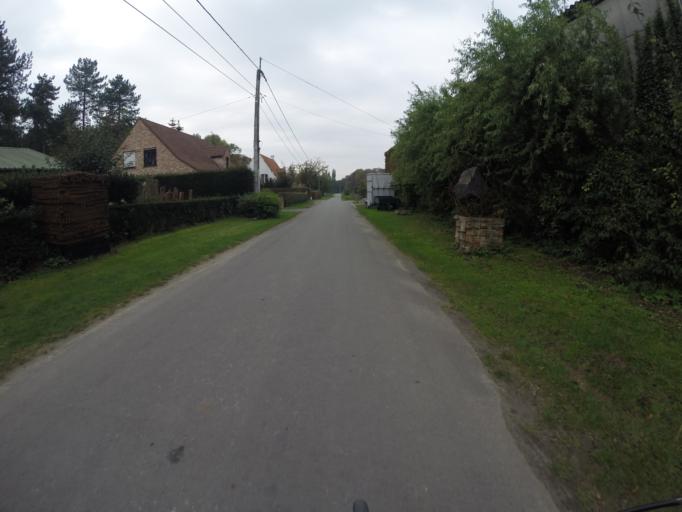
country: BE
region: Flanders
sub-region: Provincie West-Vlaanderen
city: Ruiselede
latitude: 51.0829
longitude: 3.3659
